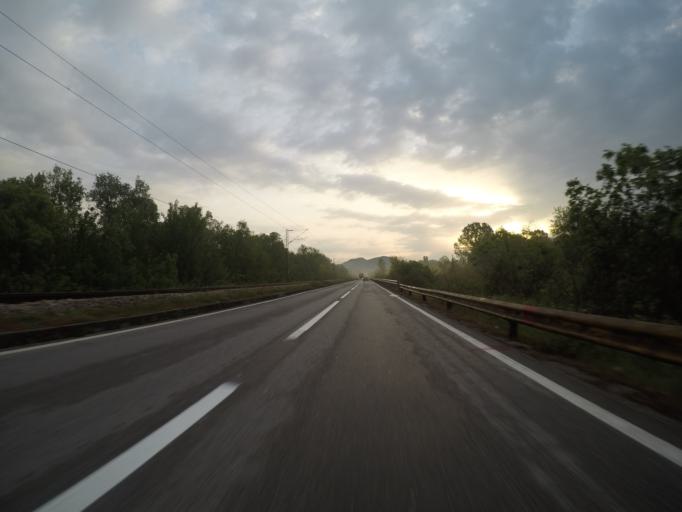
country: ME
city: Mojanovici
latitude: 42.3001
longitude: 19.1653
